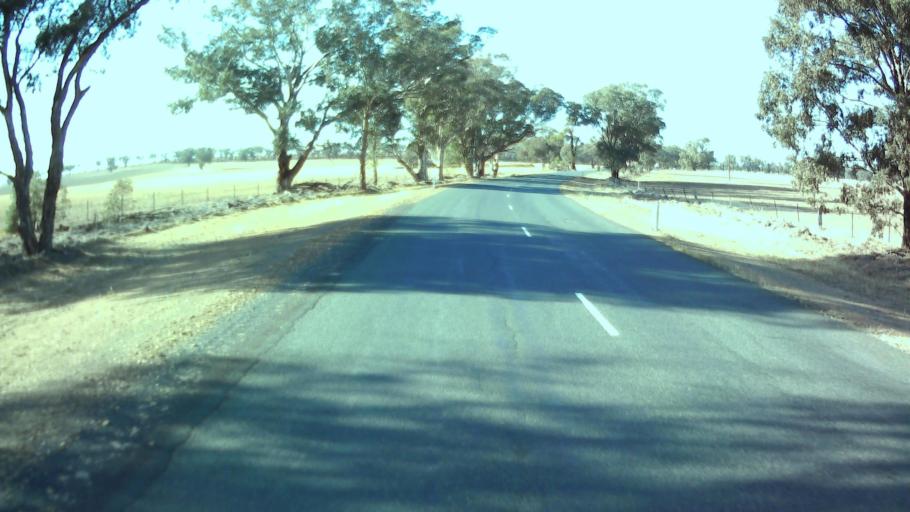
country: AU
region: New South Wales
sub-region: Weddin
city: Grenfell
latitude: -33.9343
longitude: 148.1378
